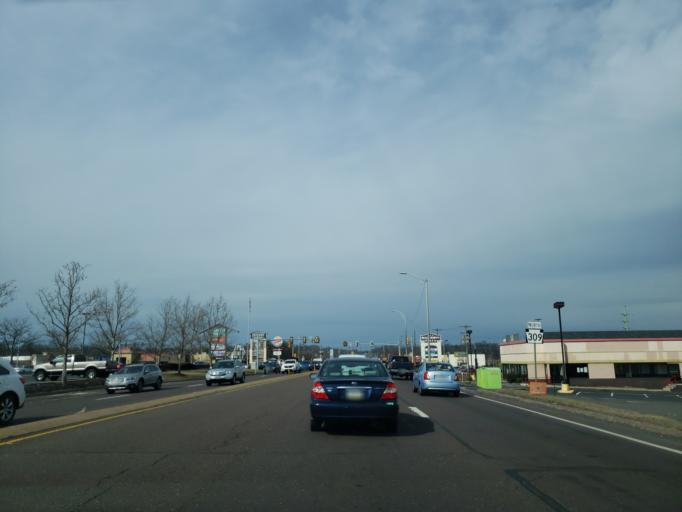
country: US
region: Pennsylvania
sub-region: Bucks County
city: Quakertown
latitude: 40.4451
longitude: -75.3592
